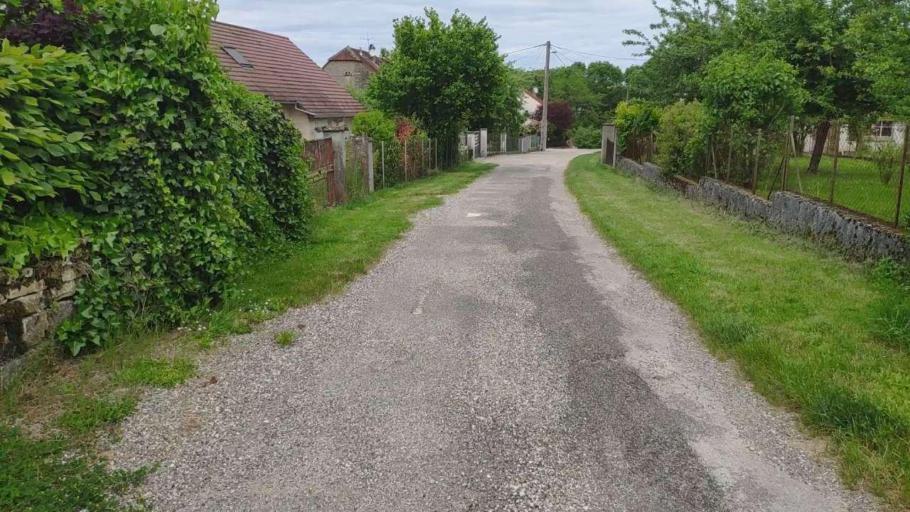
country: FR
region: Franche-Comte
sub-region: Departement du Jura
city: Montmorot
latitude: 46.7595
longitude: 5.5610
